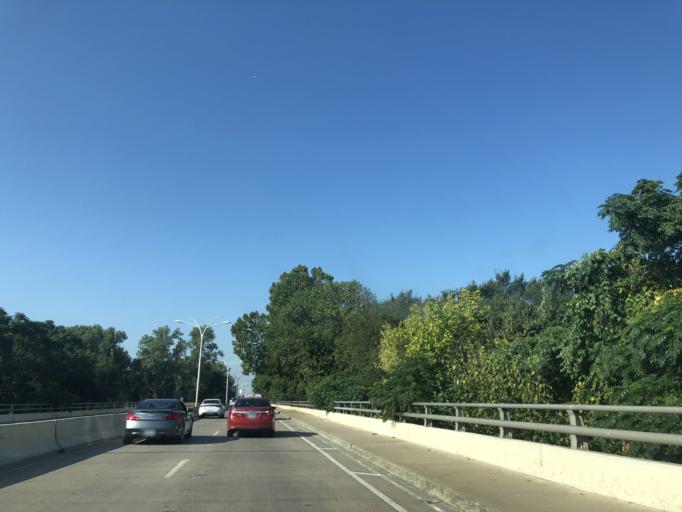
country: US
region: Texas
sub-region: Dallas County
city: Dallas
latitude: 32.7533
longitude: -96.7820
